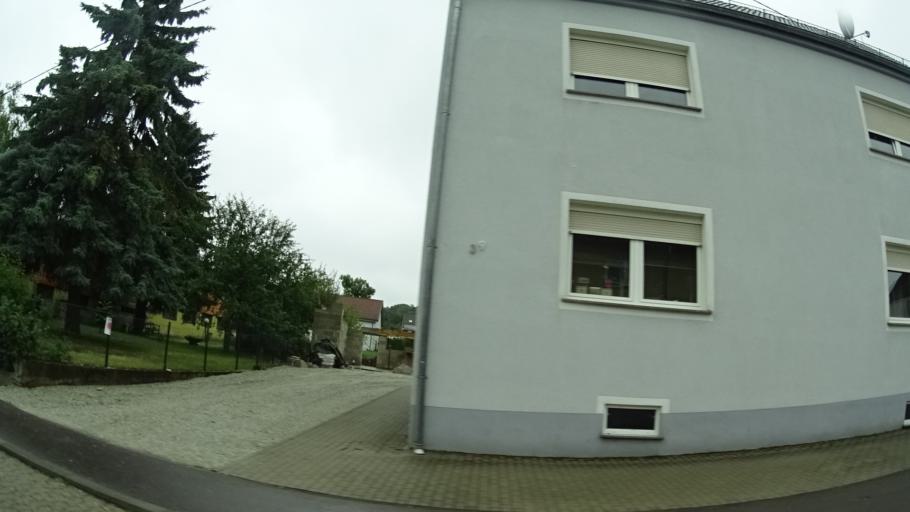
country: DE
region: Saarland
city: Quierschied
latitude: 49.3289
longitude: 6.9928
